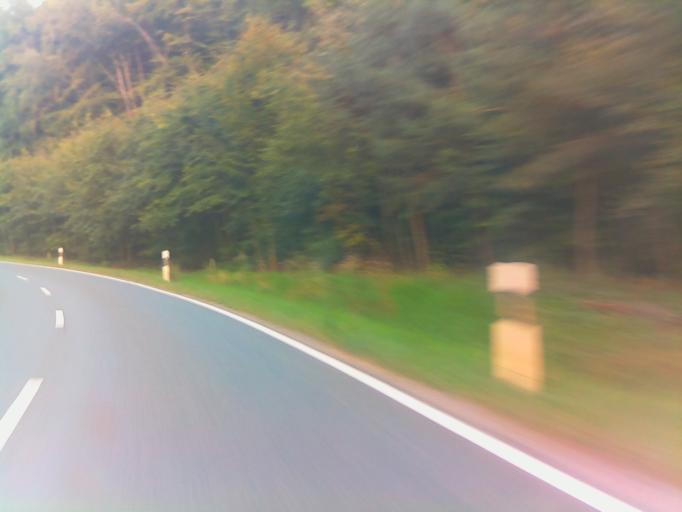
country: DE
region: Bavaria
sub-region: Regierungsbezirk Unterfranken
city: Ramsthal
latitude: 50.1480
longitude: 10.0975
